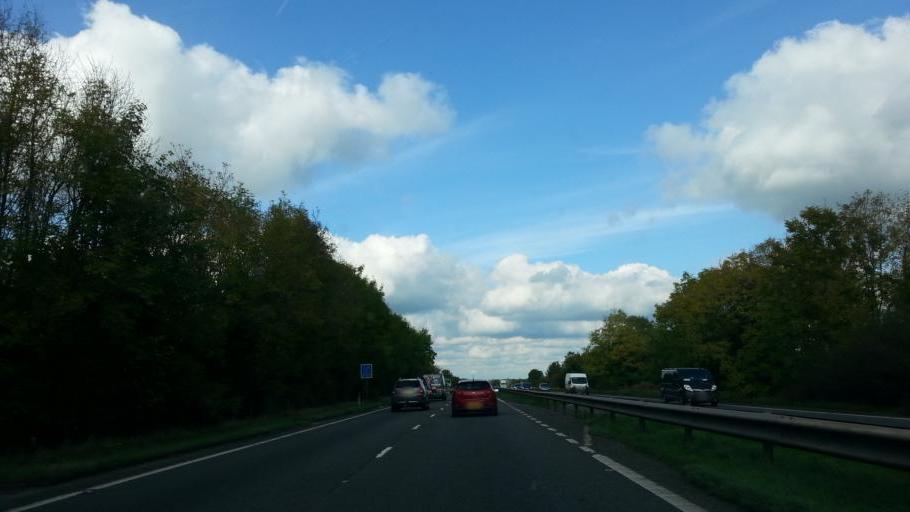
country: GB
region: England
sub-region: Derbyshire
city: Alfreton
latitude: 53.0773
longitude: -1.4089
